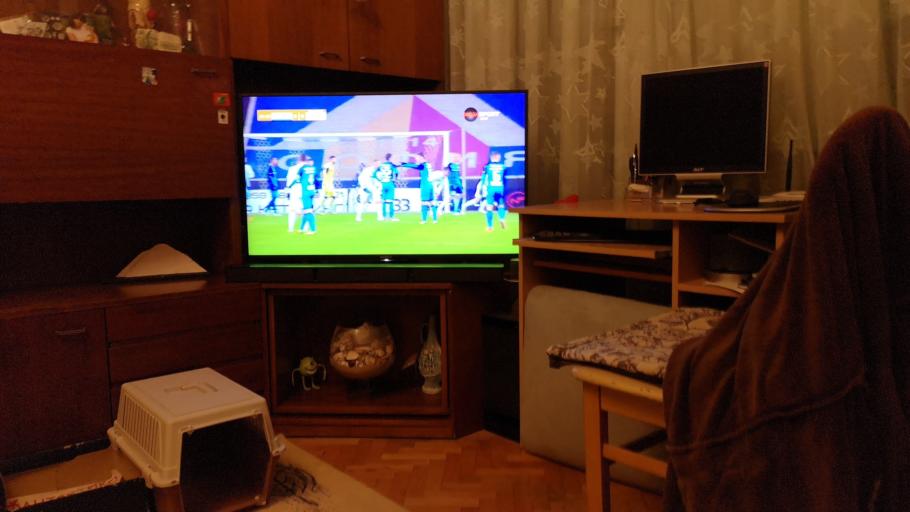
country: BG
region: Sofiya
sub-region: Obshtina Bozhurishte
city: Bozhurishte
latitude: 42.7157
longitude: 23.2477
